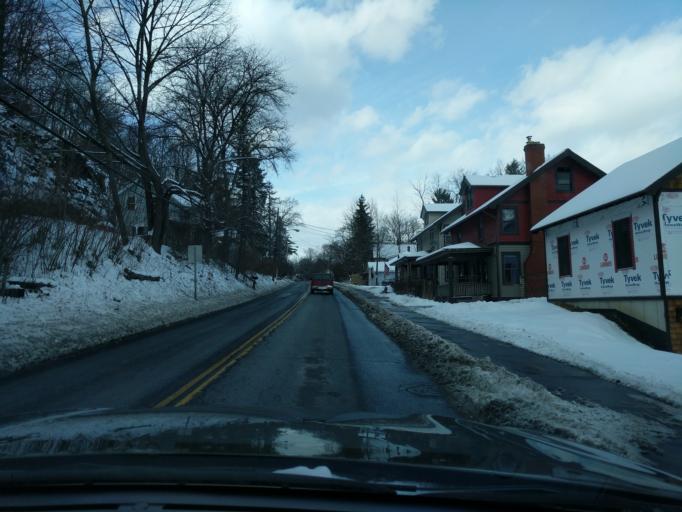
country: US
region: New York
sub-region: Tompkins County
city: Ithaca
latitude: 42.4464
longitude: -76.5164
